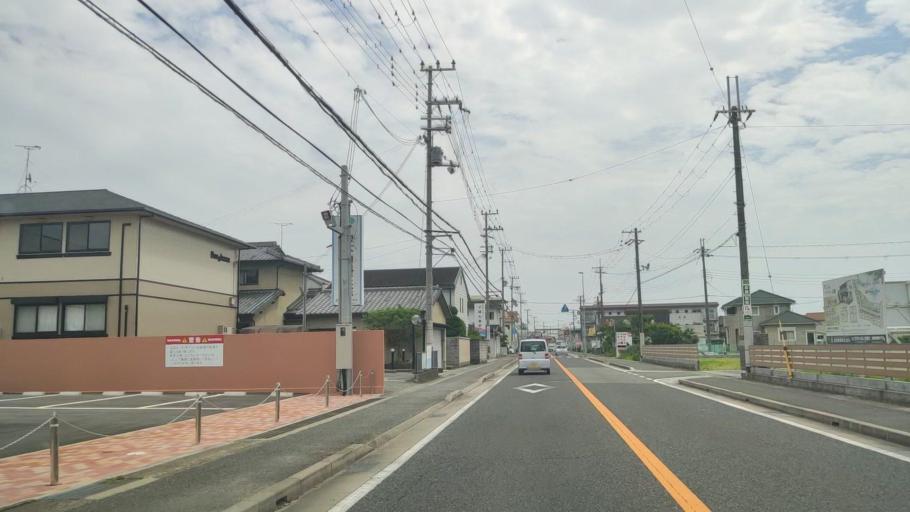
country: JP
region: Hyogo
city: Tatsunocho-tominaga
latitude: 34.8707
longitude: 134.5541
